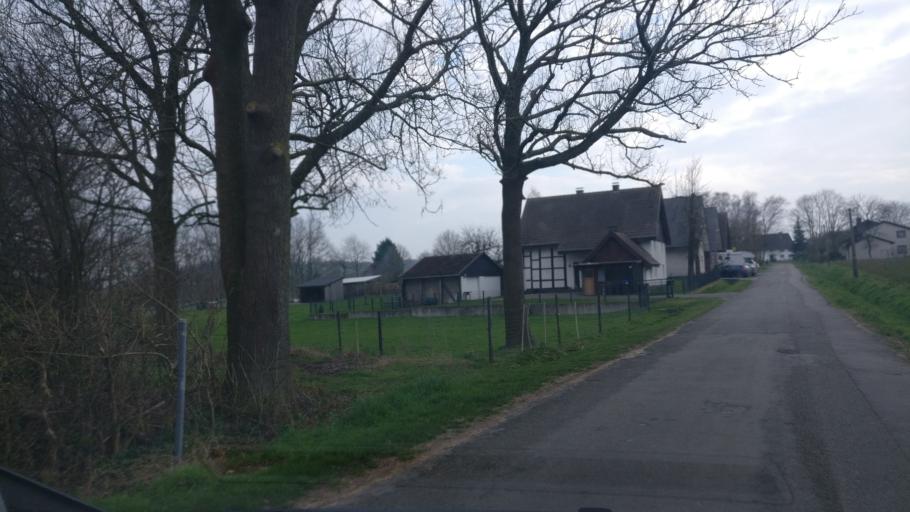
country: DE
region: North Rhine-Westphalia
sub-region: Regierungsbezirk Detmold
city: Lage
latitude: 52.0156
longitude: 8.7842
